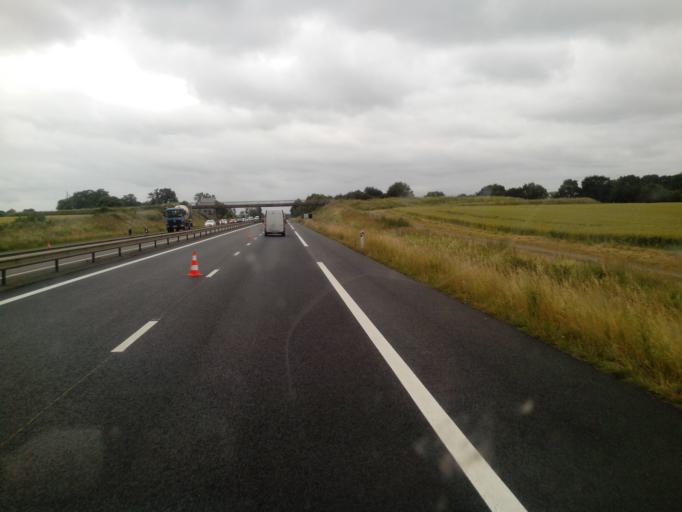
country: FR
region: Brittany
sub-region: Departement d'Ille-et-Vilaine
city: Chatillon-sur-Seiche
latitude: 48.0720
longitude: -1.6763
